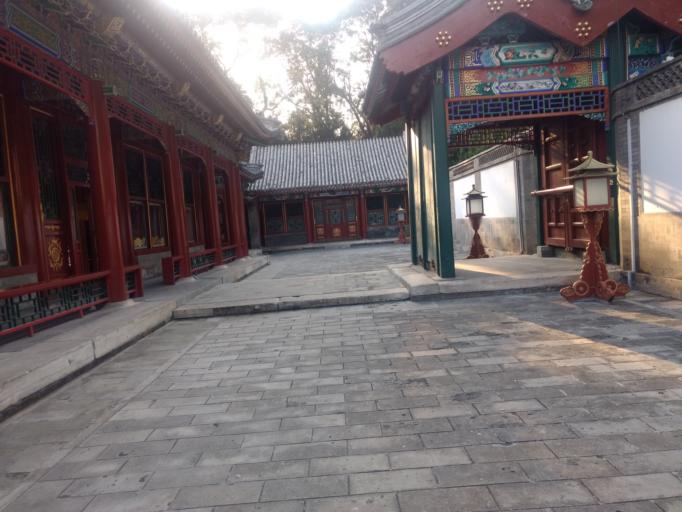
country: CN
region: Beijing
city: Haidian
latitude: 39.9979
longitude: 116.2737
